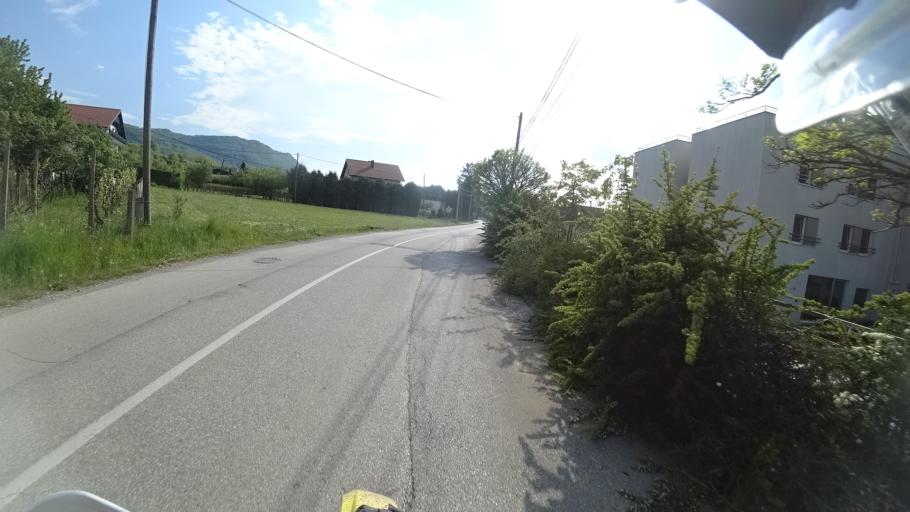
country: HR
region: Zagrebacka
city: Jablanovec
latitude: 45.8897
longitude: 15.8693
